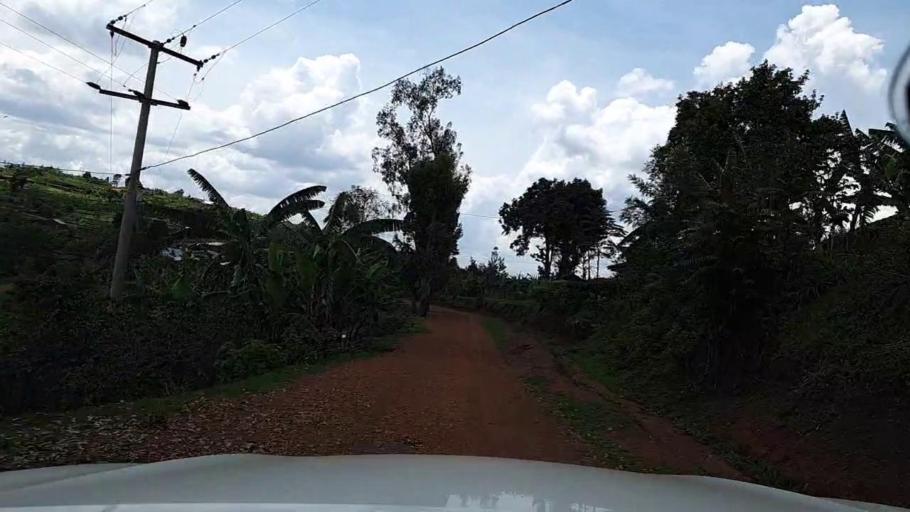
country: RW
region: Southern Province
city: Butare
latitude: -2.7605
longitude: 29.7456
